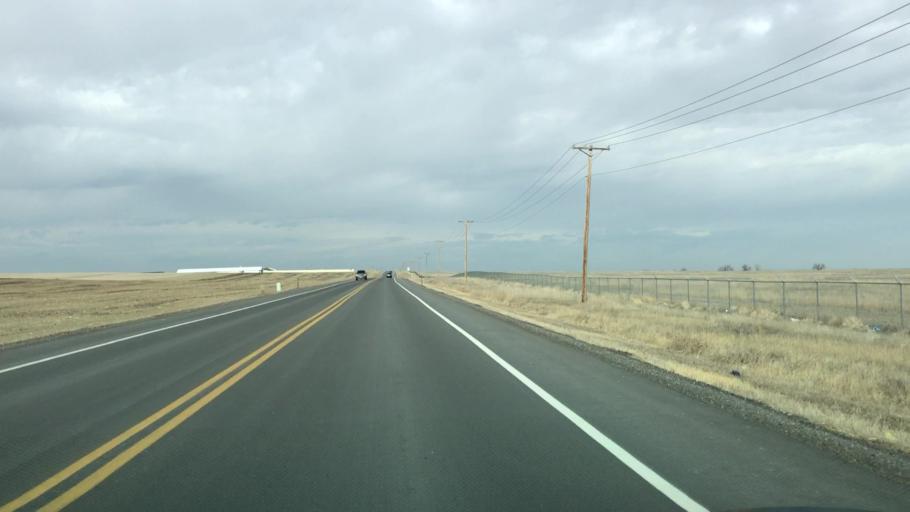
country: US
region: Colorado
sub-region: Larimer County
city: Loveland
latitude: 40.4505
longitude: -105.0198
